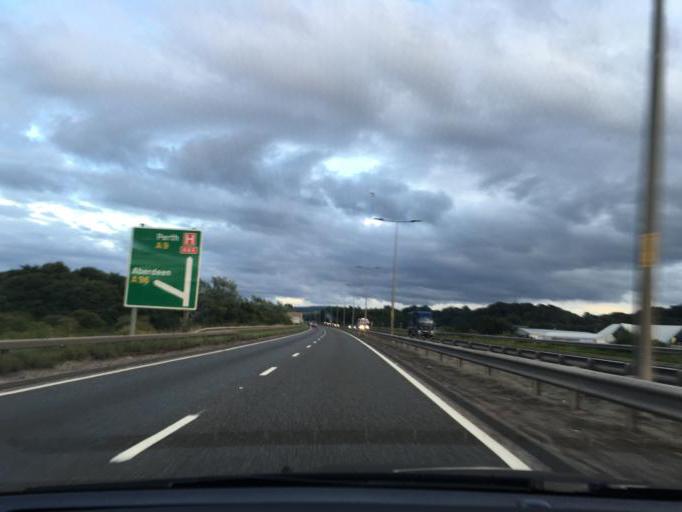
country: GB
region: Scotland
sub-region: Highland
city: Inverness
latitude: 57.4865
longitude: -4.2056
